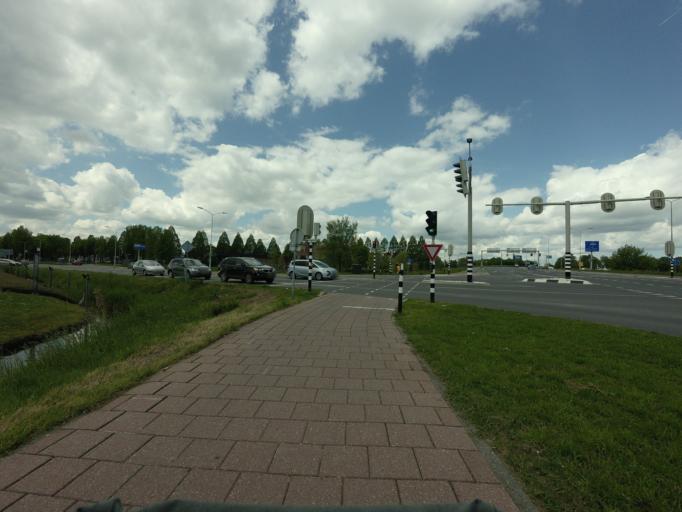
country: NL
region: North Brabant
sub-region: Gemeente Woudrichem
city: Woudrichem
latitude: 51.8405
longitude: 5.0035
